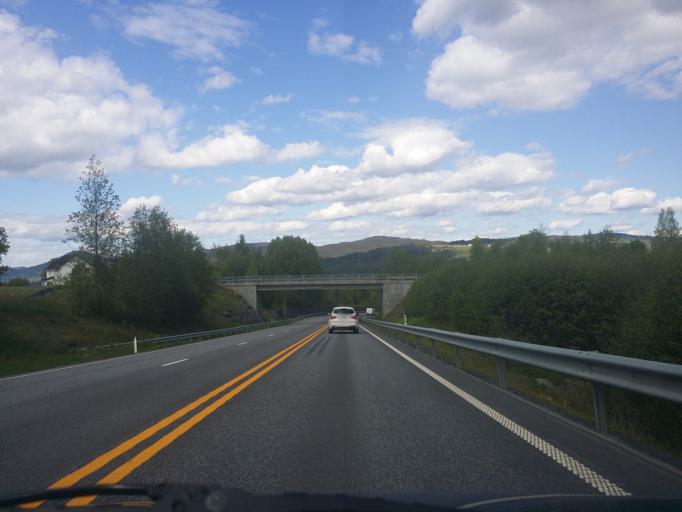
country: NO
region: Oppland
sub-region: Lunner
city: Roa
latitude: 60.2945
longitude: 10.5796
